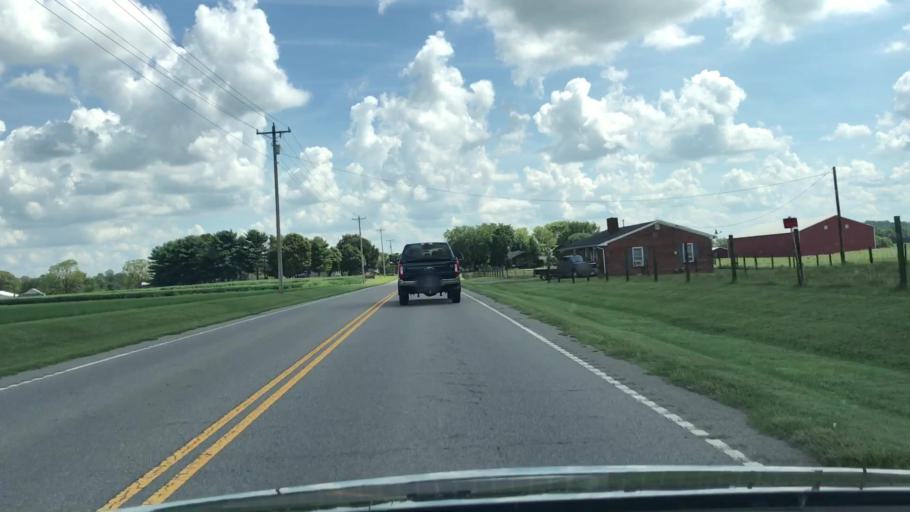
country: US
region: Tennessee
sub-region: Robertson County
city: Cross Plains
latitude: 36.5548
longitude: -86.7891
